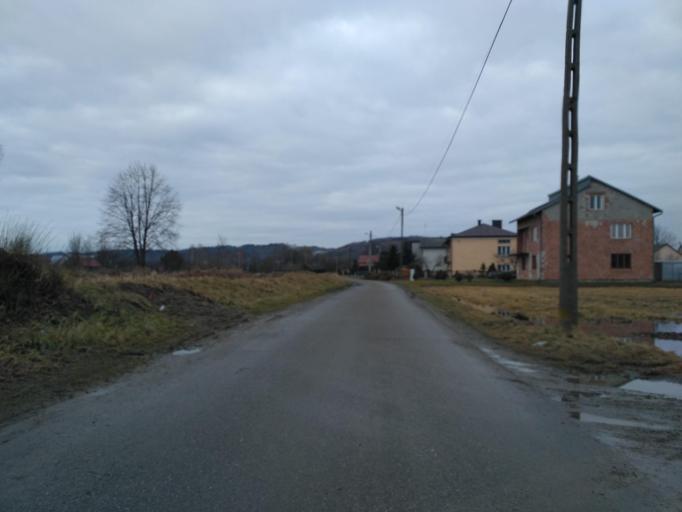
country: PL
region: Subcarpathian Voivodeship
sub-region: Powiat przemyski
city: Dubiecko
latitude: 49.8292
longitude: 22.3803
